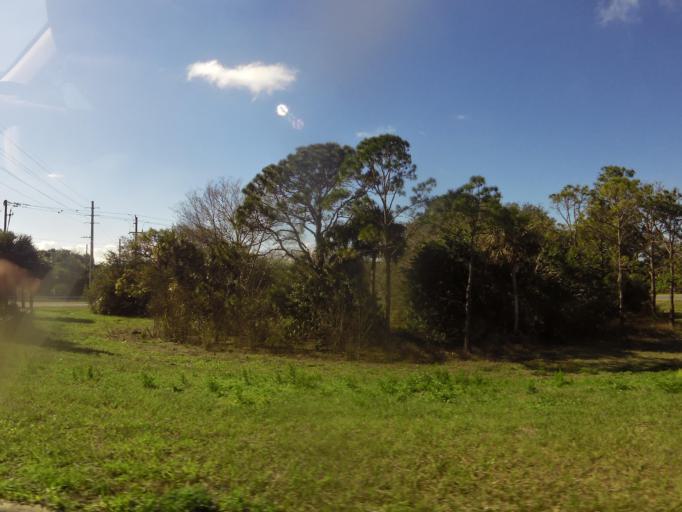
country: US
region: Florida
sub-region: Brevard County
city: Port Saint John
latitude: 28.5284
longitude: -80.7883
